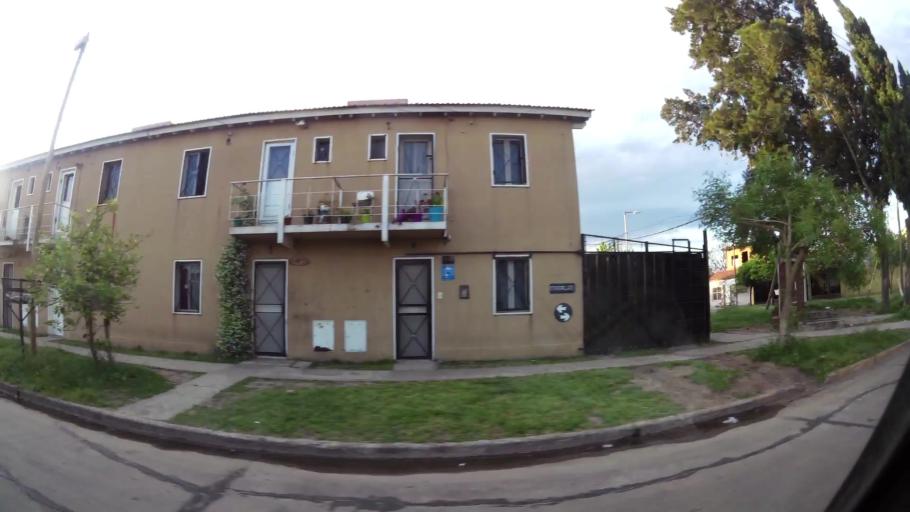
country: AR
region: Buenos Aires
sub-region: Partido de Lanus
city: Lanus
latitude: -34.7157
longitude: -58.3415
